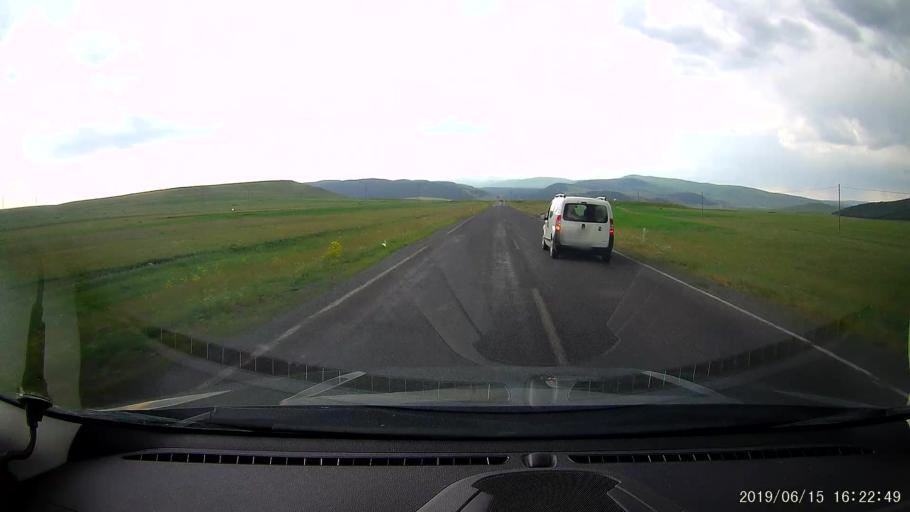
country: TR
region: Ardahan
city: Hanak
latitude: 41.1844
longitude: 42.8550
